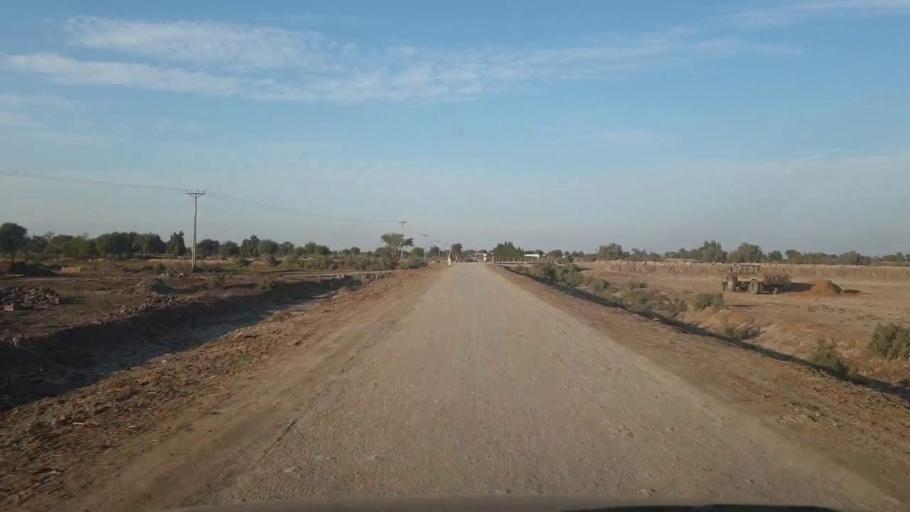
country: PK
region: Sindh
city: Sinjhoro
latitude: 26.0313
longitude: 68.8352
